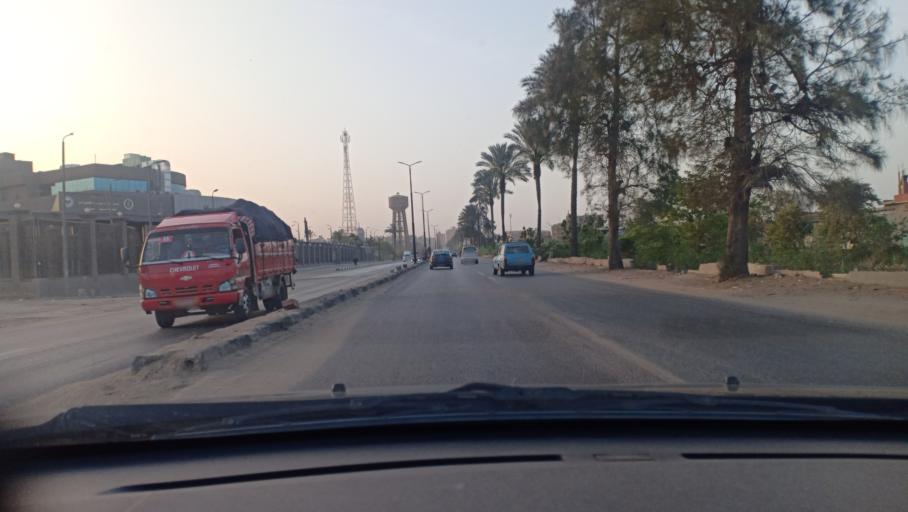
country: EG
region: Muhafazat al Gharbiyah
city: Zifta
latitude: 30.6982
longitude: 31.2748
